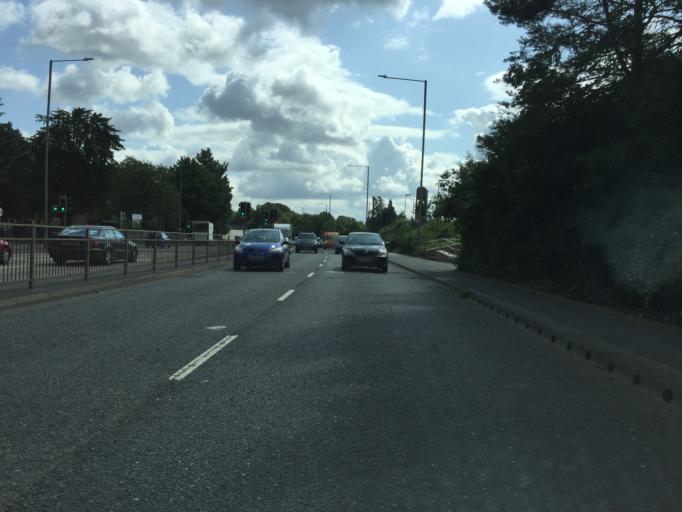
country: GB
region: England
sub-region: Kent
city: Aylesford
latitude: 51.2929
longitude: 0.4754
